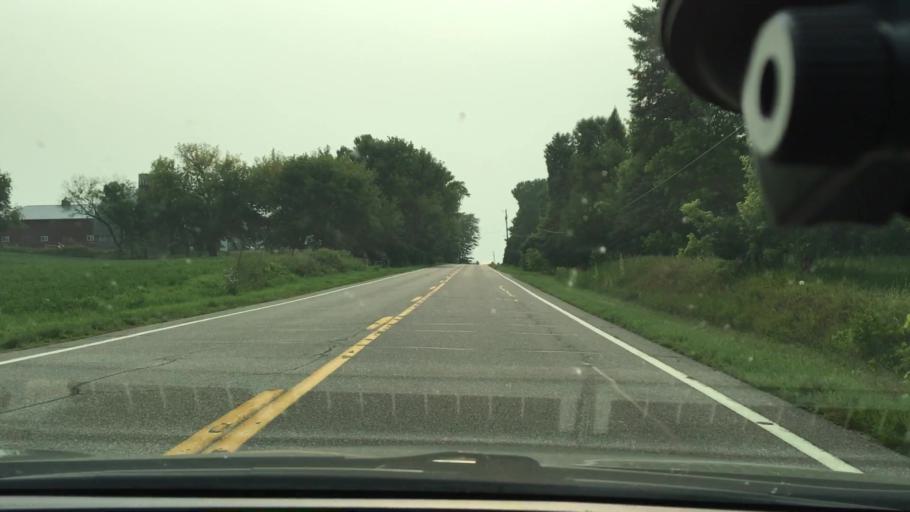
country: US
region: Minnesota
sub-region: Hennepin County
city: Dayton
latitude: 45.2235
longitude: -93.4752
